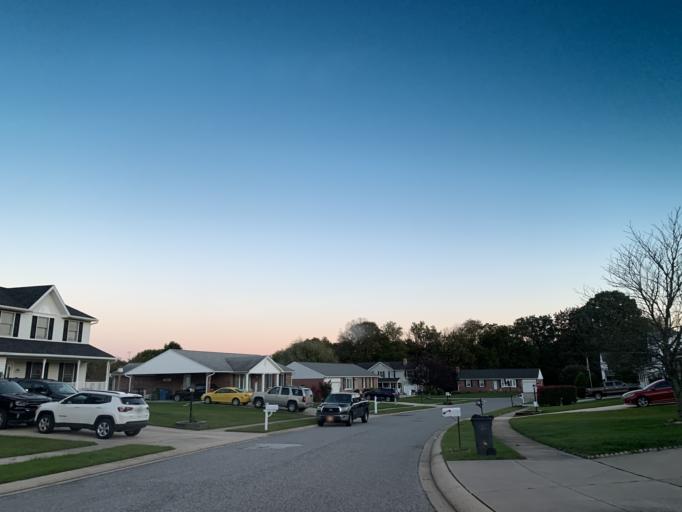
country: US
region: Maryland
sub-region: Harford County
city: South Bel Air
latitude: 39.5448
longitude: -76.3019
